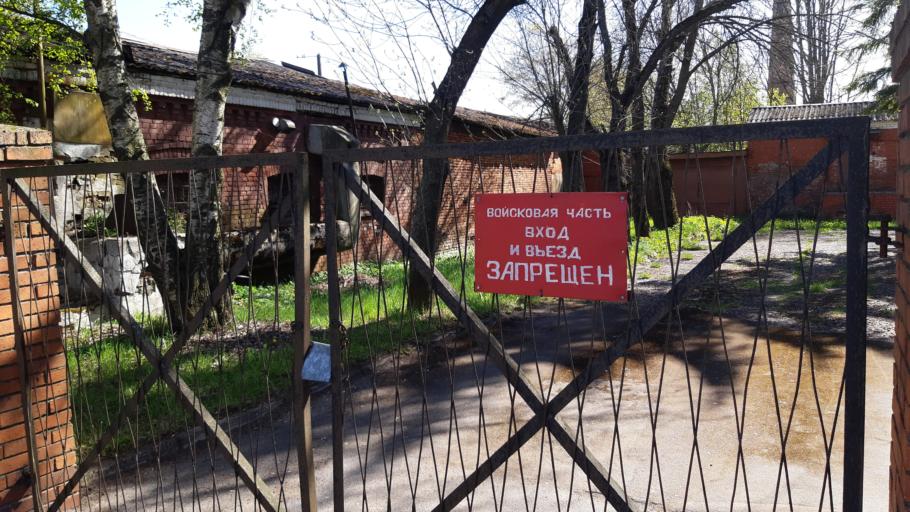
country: RU
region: St.-Petersburg
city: Kronshtadt
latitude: 60.0015
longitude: 29.7611
